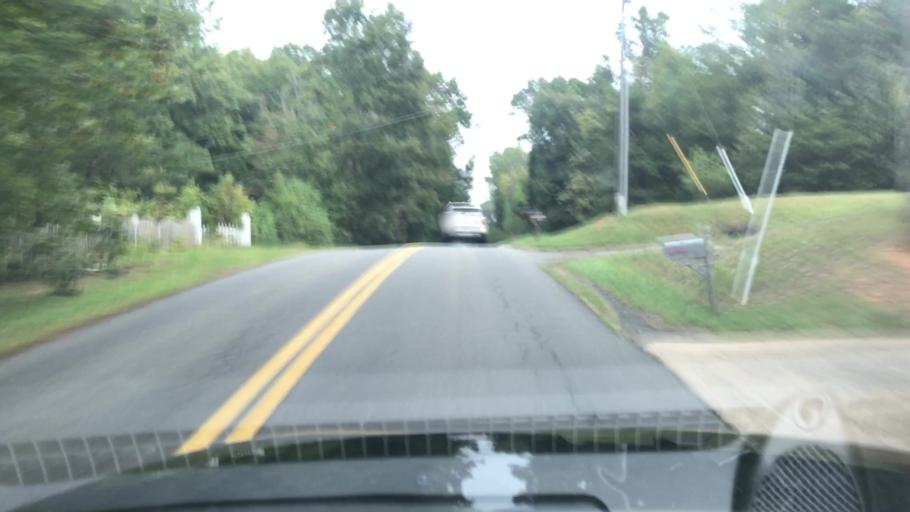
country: US
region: Virginia
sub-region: Fauquier County
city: New Baltimore
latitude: 38.7169
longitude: -77.6633
